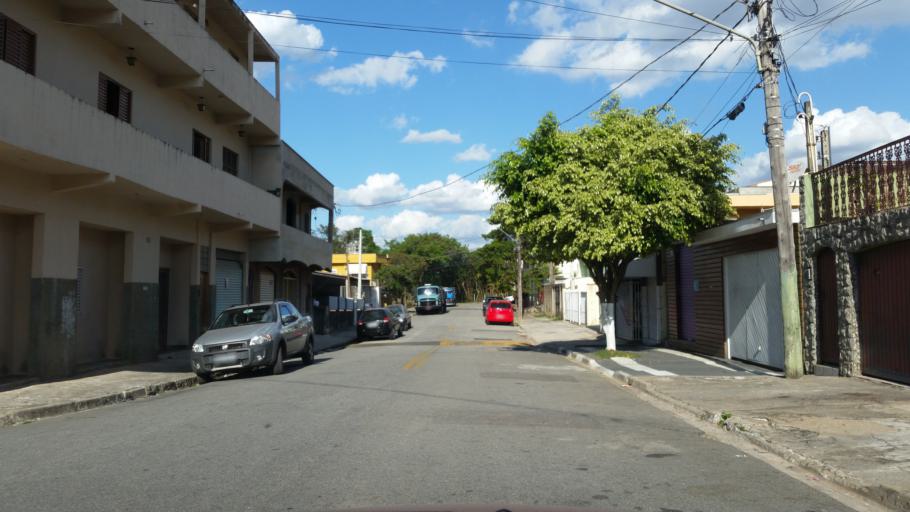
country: BR
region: Sao Paulo
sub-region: Mairinque
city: Mairinque
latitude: -23.5173
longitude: -47.2595
